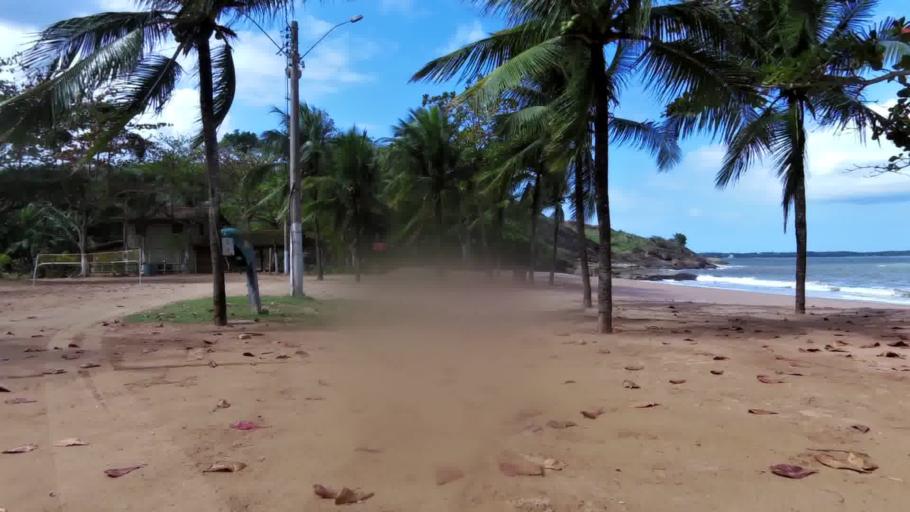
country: BR
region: Espirito Santo
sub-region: Piuma
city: Piuma
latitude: -20.8101
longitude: -40.6613
